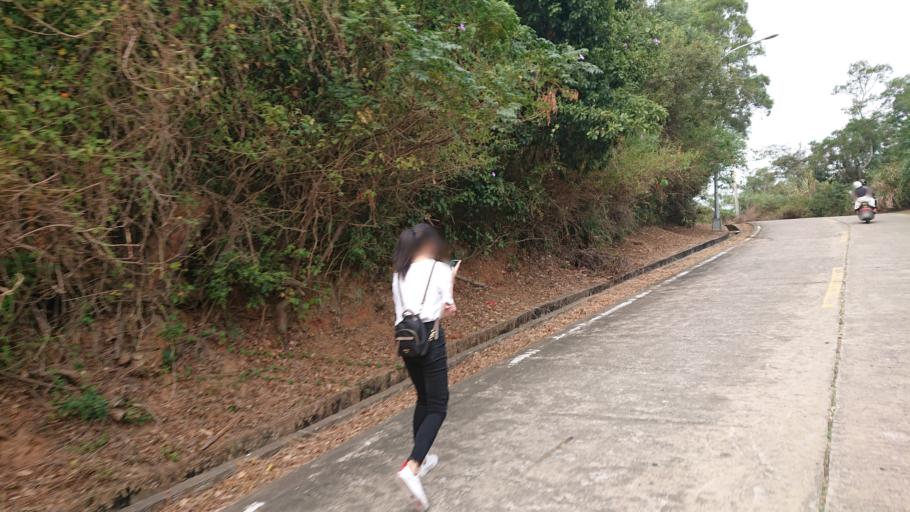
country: TW
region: Fukien
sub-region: Kinmen
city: Jincheng
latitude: 24.4407
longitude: 118.2509
